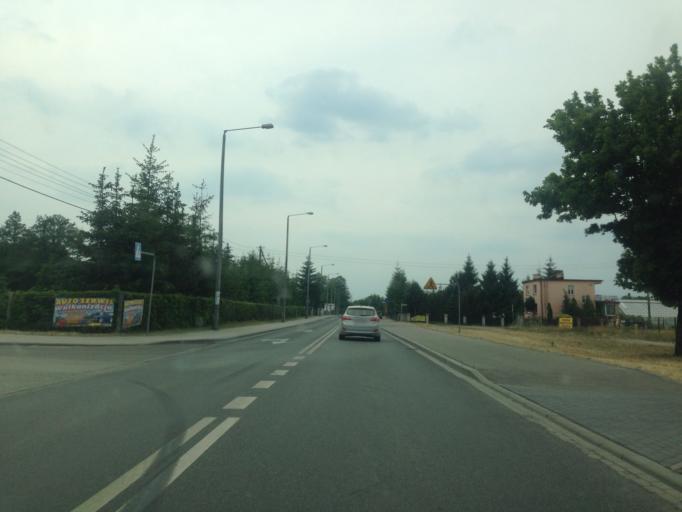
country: PL
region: Kujawsko-Pomorskie
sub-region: Powiat grudziadzki
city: Rogozno
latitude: 53.5021
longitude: 18.8523
